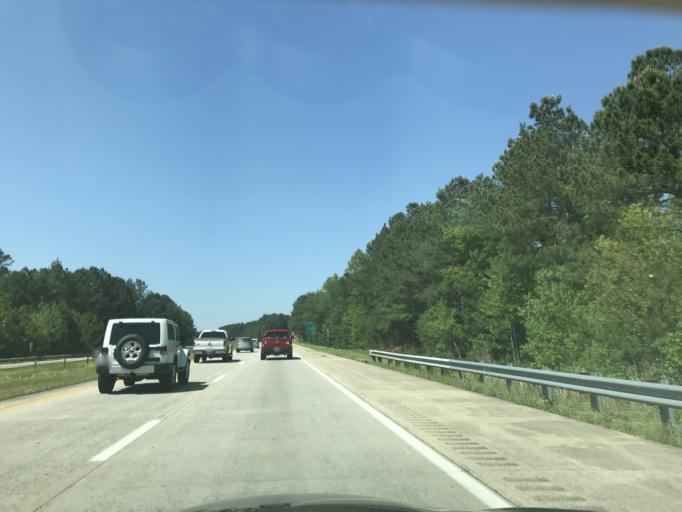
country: US
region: North Carolina
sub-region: Johnston County
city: Benson
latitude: 35.5106
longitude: -78.5557
